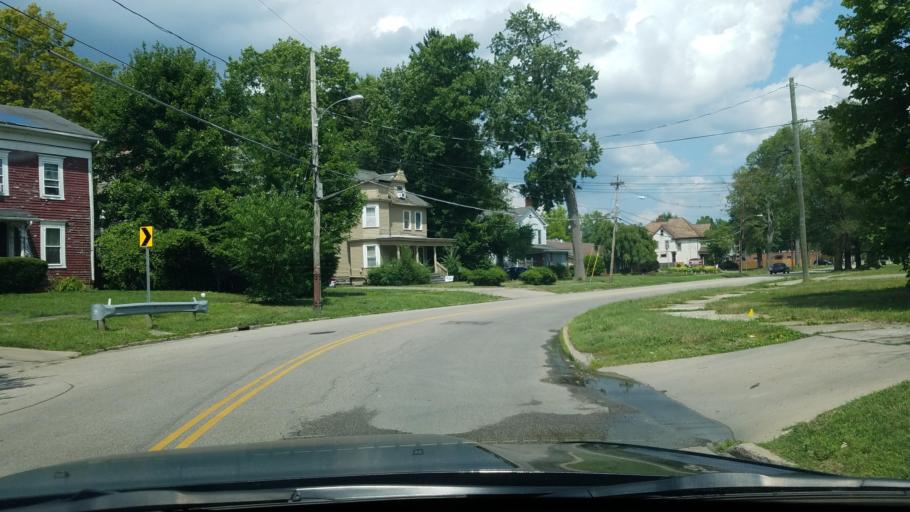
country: US
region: Ohio
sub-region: Trumbull County
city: Warren
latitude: 41.2417
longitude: -80.8218
